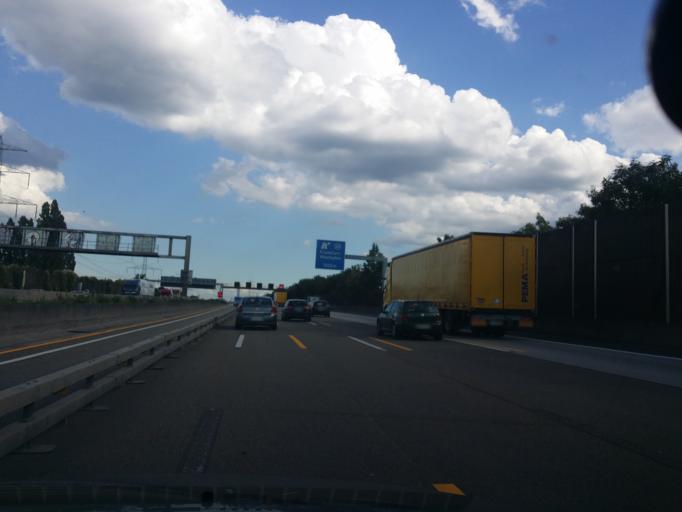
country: DE
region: Hesse
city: Niederrad
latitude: 50.1027
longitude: 8.6076
